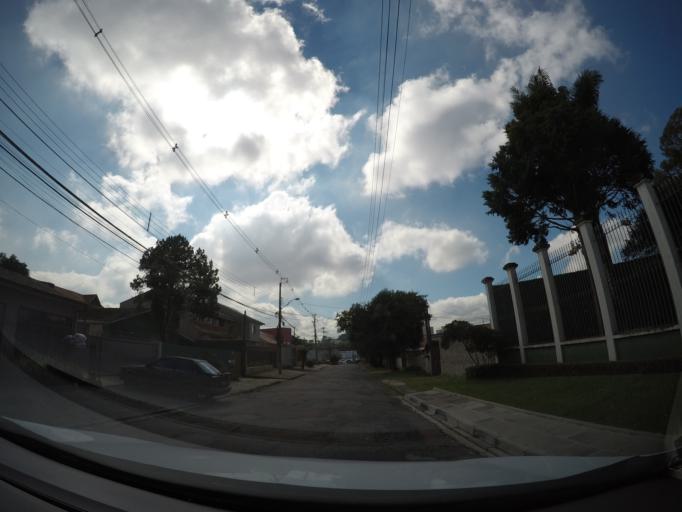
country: BR
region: Parana
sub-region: Sao Jose Dos Pinhais
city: Sao Jose dos Pinhais
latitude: -25.4895
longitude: -49.2242
